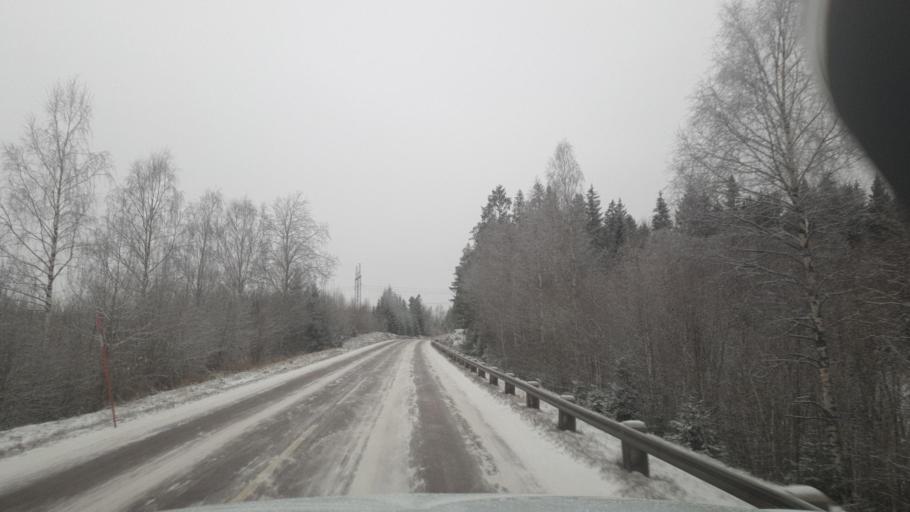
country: SE
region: Vaermland
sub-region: Grums Kommun
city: Slottsbron
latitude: 59.4144
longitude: 12.9902
